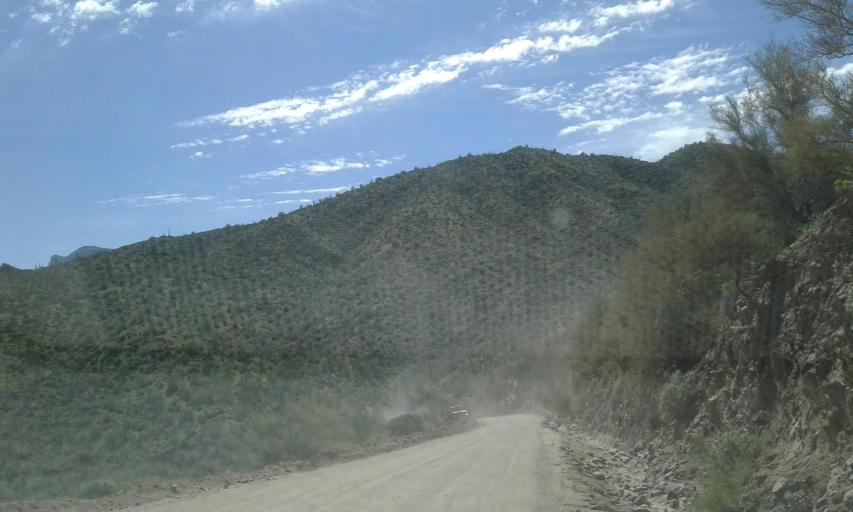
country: US
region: Arizona
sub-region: Gila County
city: Tonto Basin
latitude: 33.5980
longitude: -111.2045
